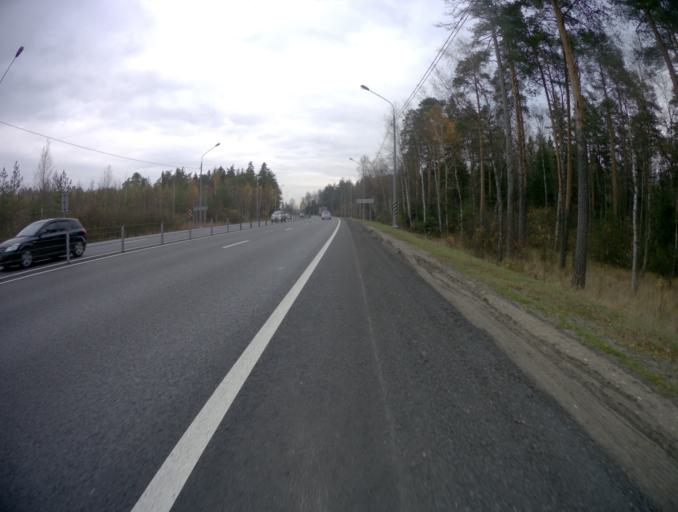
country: RU
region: Moskovskaya
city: Malaya Dubna
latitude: 55.8668
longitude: 38.9638
